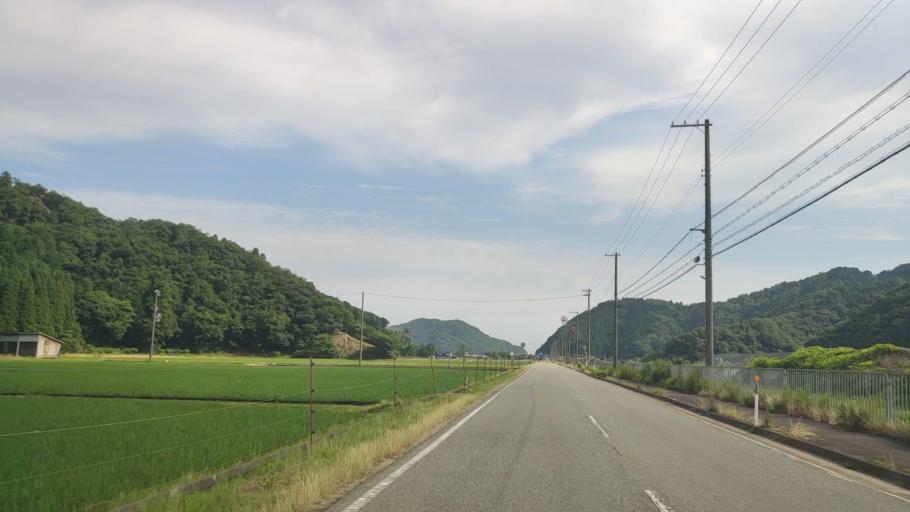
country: JP
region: Hyogo
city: Toyooka
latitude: 35.6267
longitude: 134.8411
